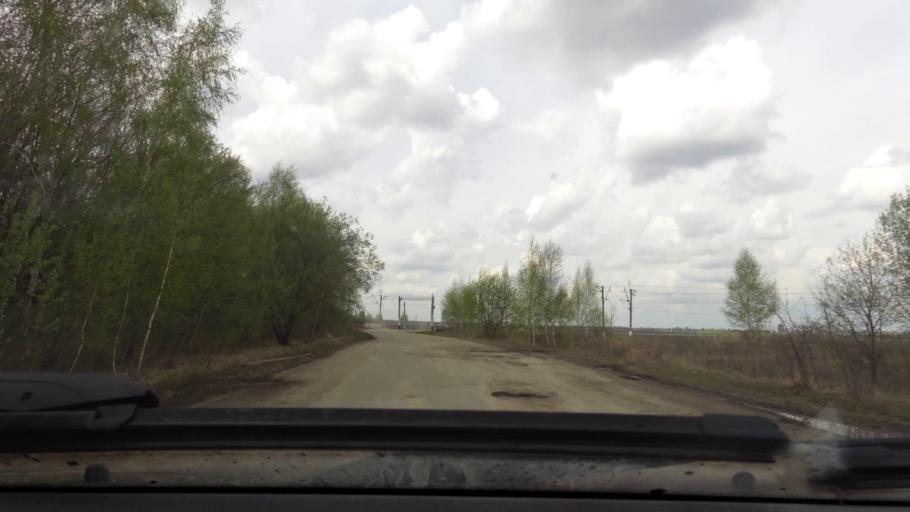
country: RU
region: Rjazan
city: Bagramovo
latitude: 54.7064
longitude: 39.3159
